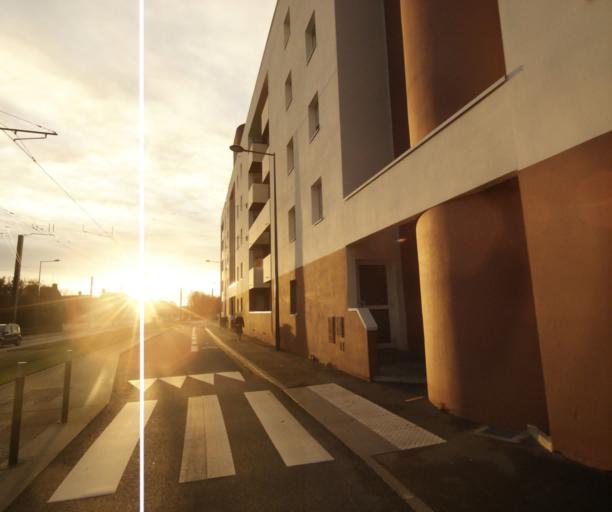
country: FR
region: Pays de la Loire
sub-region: Departement de la Sarthe
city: Coulaines
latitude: 48.0184
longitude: 0.2175
